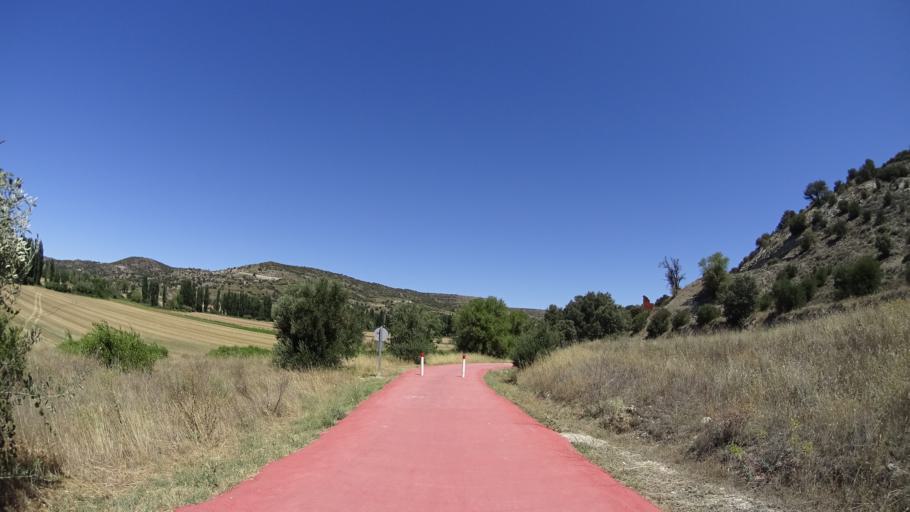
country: ES
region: Madrid
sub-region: Provincia de Madrid
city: Ambite
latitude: 40.3142
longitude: -3.1894
